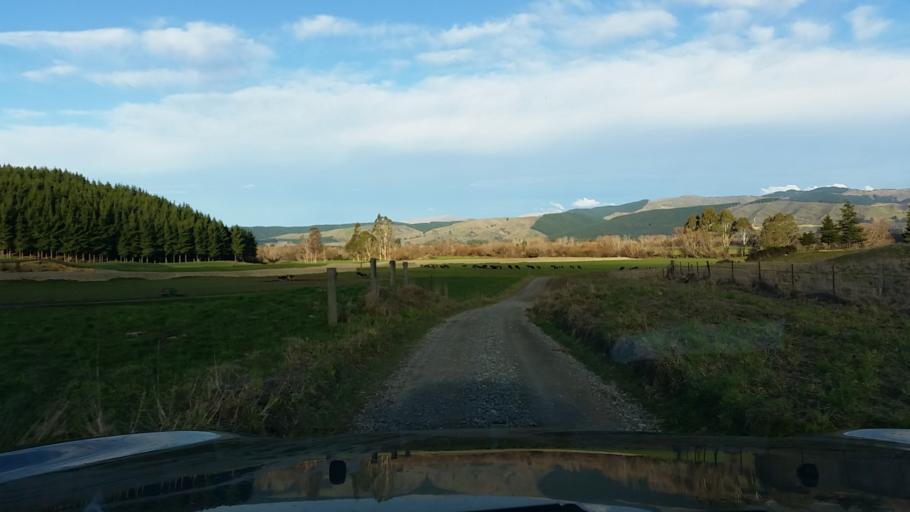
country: NZ
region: Nelson
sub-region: Nelson City
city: Nelson
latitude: -41.5399
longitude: 173.4949
